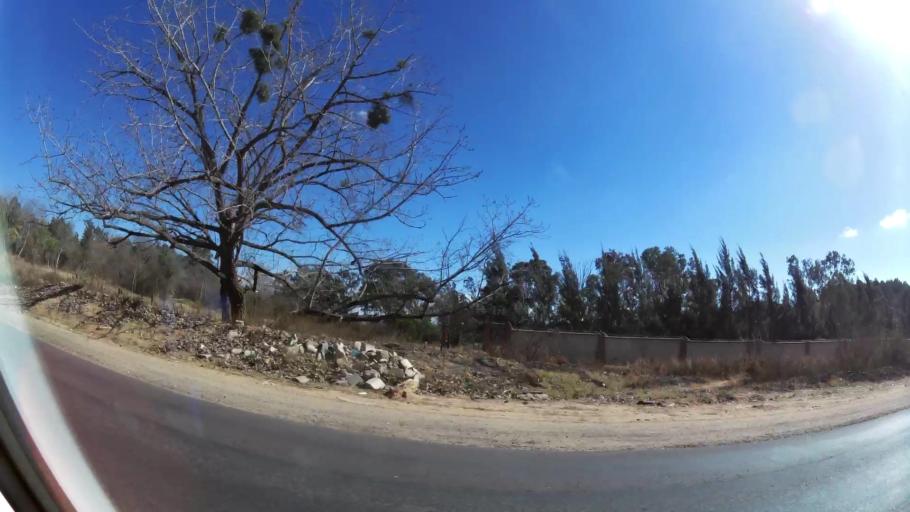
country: ZA
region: Gauteng
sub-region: City of Johannesburg Metropolitan Municipality
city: Midrand
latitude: -25.9618
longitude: 28.0821
